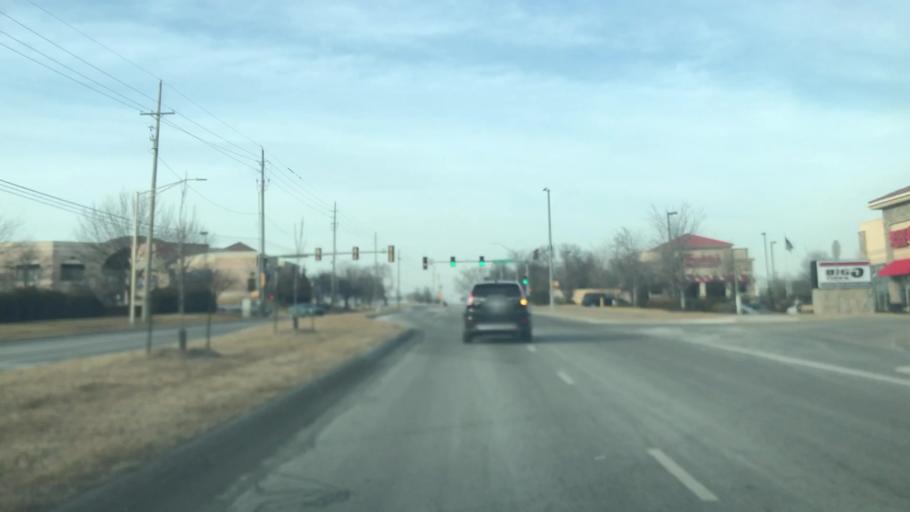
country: US
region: Kansas
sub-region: Johnson County
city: Lenexa
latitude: 38.9134
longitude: -94.7610
